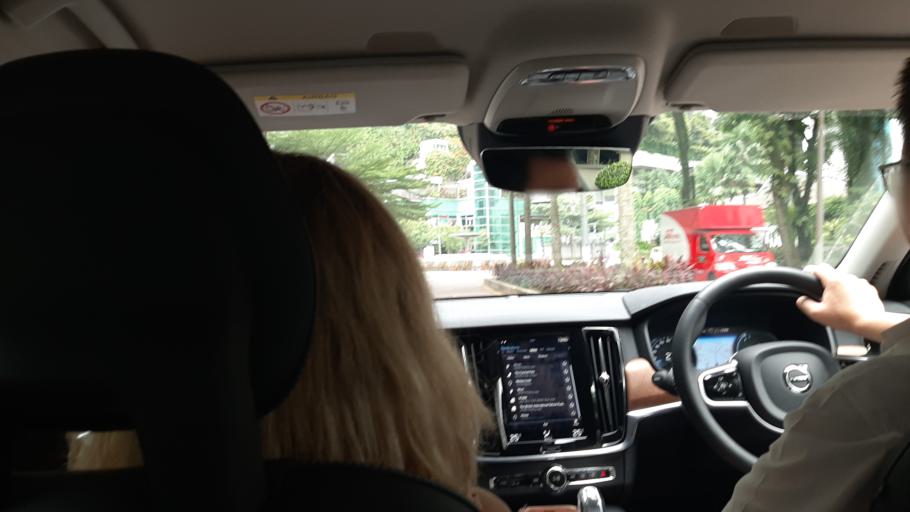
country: MY
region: Kuala Lumpur
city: Kuala Lumpur
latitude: 3.1697
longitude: 101.6544
